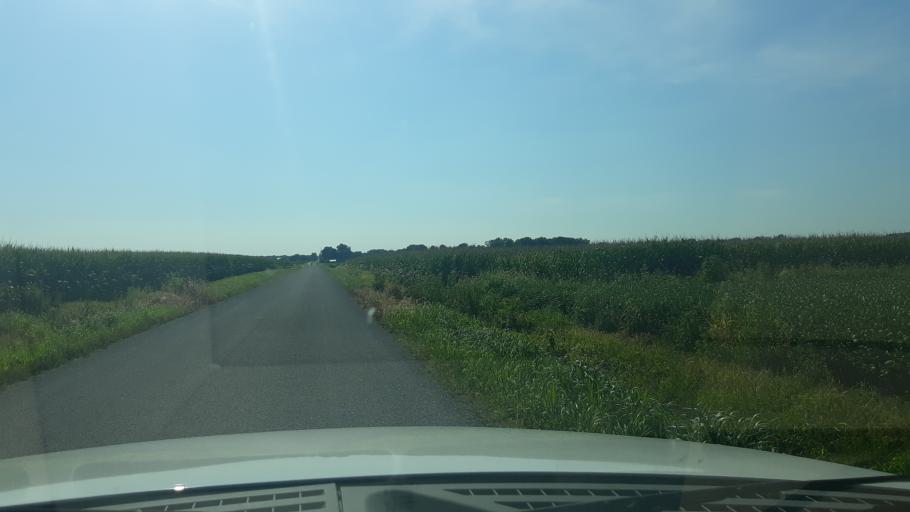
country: US
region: Illinois
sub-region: Saline County
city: Eldorado
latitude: 37.8633
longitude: -88.4935
